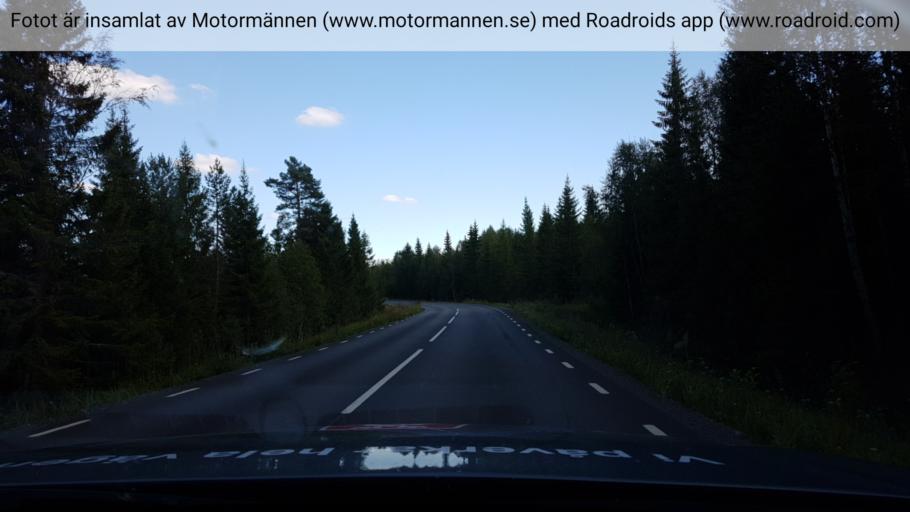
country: SE
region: Jaemtland
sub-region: OEstersunds Kommun
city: Lit
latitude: 63.3763
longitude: 14.8194
